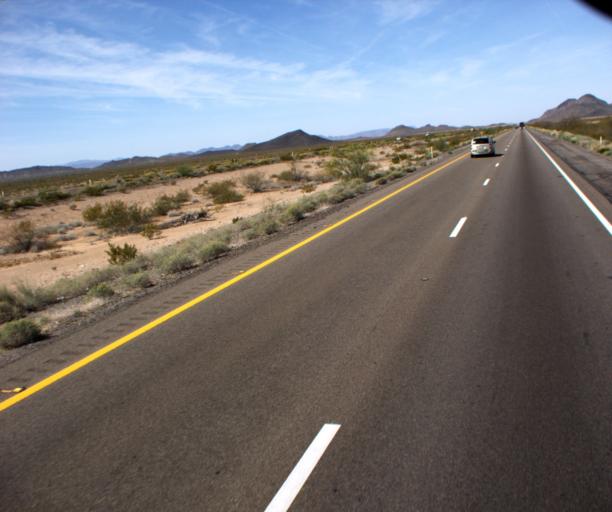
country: US
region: Arizona
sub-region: La Paz County
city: Salome
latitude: 33.6026
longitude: -113.5743
